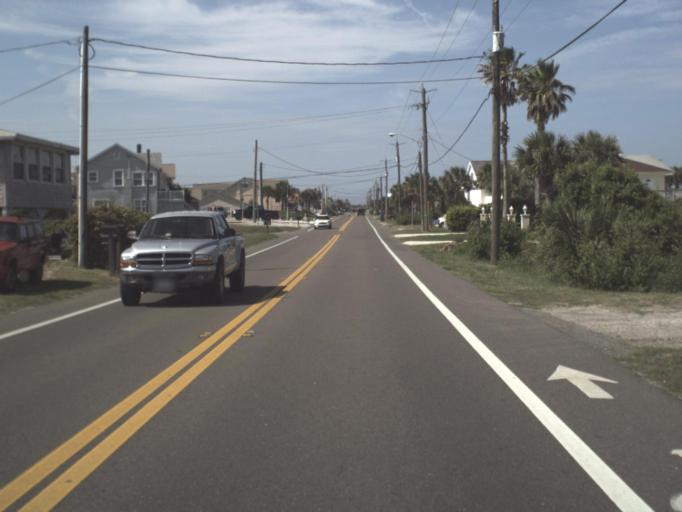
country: US
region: Florida
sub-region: Nassau County
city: Fernandina Beach
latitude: 30.6297
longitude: -81.4390
